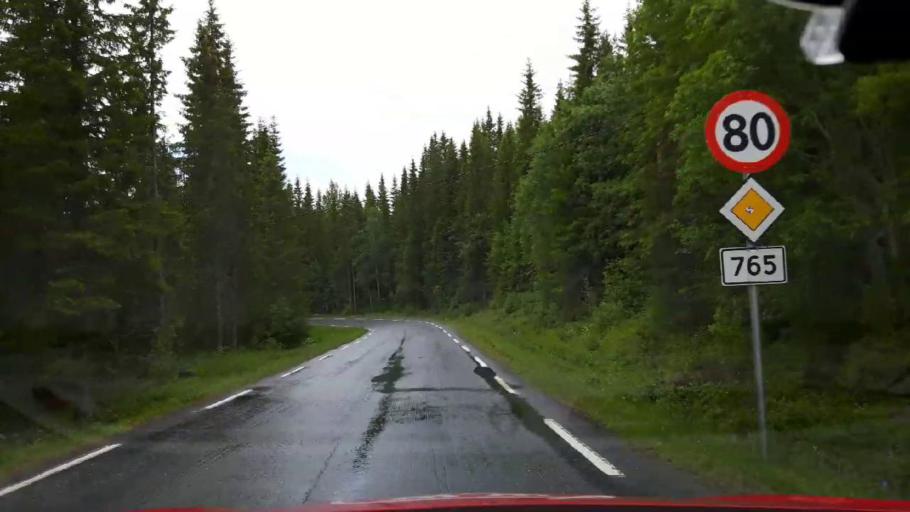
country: NO
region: Nord-Trondelag
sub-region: Lierne
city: Sandvika
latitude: 64.0917
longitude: 14.0517
